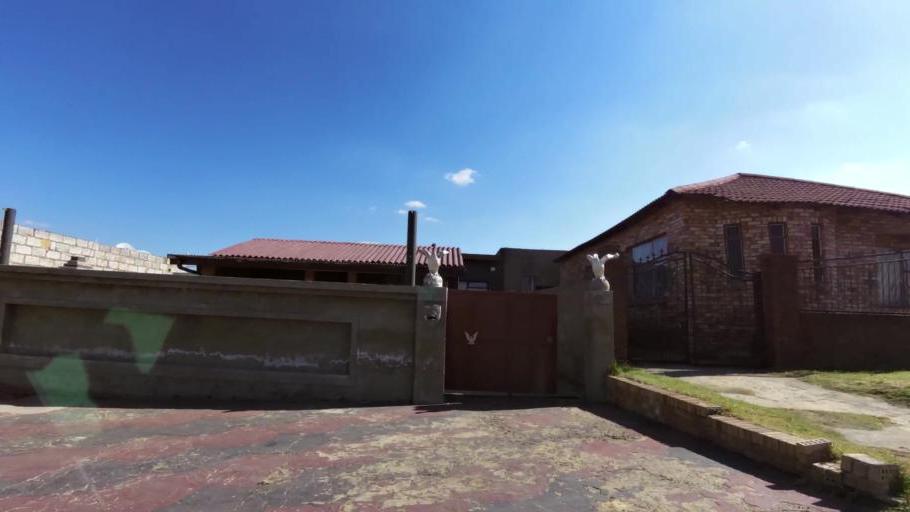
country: ZA
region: Gauteng
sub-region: City of Johannesburg Metropolitan Municipality
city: Soweto
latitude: -26.2436
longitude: 27.9042
